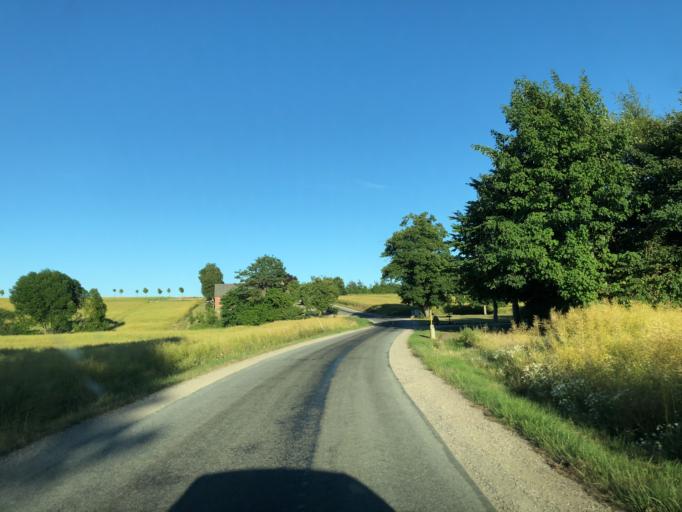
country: DK
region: Central Jutland
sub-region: Horsens Kommune
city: Horsens
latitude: 55.9231
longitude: 9.8727
